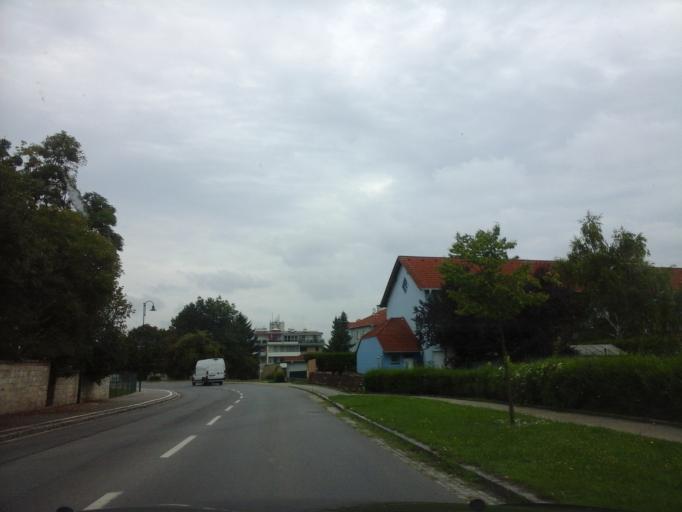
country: AT
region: Lower Austria
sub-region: Politischer Bezirk Ganserndorf
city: Orth an der Donau
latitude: 48.1463
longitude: 16.6990
